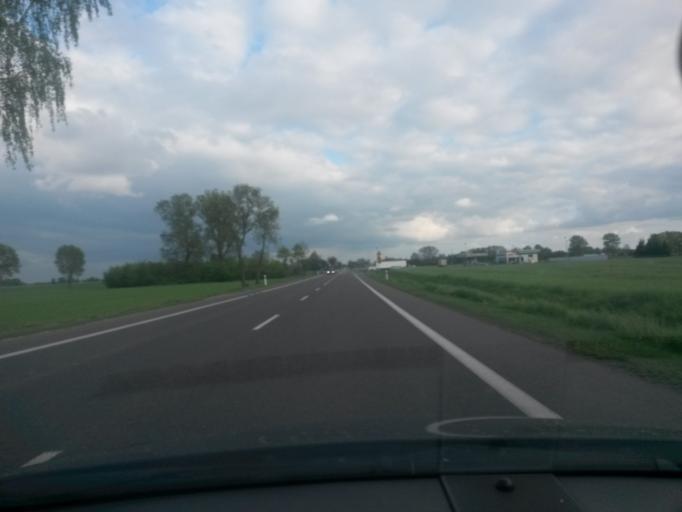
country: PL
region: Masovian Voivodeship
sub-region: Powiat plocki
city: Drobin
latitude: 52.7052
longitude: 20.0341
